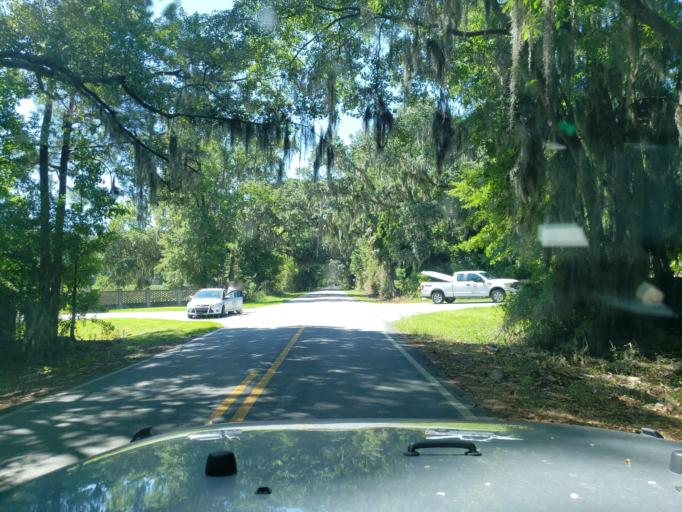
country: US
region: Georgia
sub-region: Chatham County
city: Georgetown
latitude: 31.9562
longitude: -81.2164
